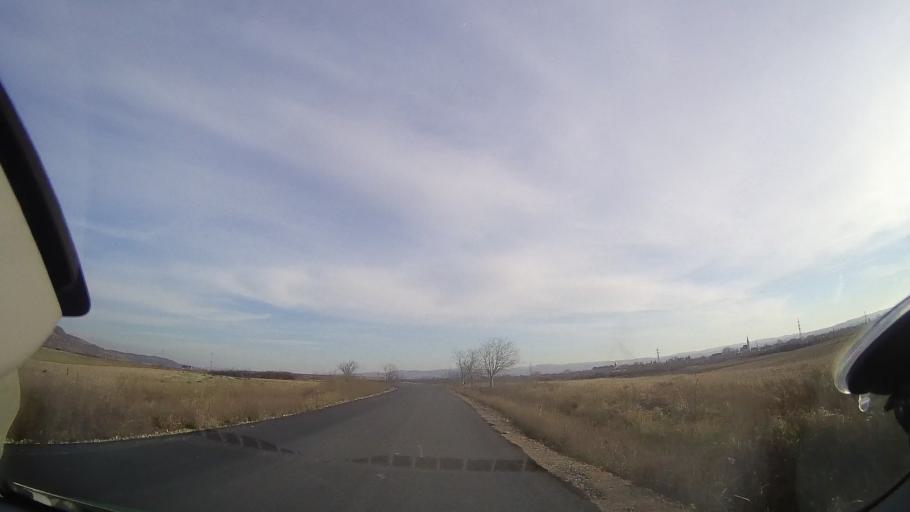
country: RO
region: Bihor
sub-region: Comuna Tileagd
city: Tileagd
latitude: 47.0843
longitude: 22.1860
